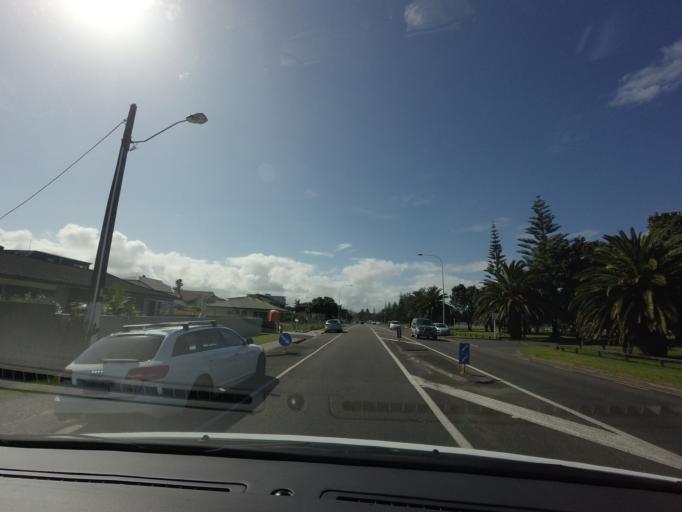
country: NZ
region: Auckland
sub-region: Auckland
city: Rothesay Bay
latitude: -36.5920
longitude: 174.6985
